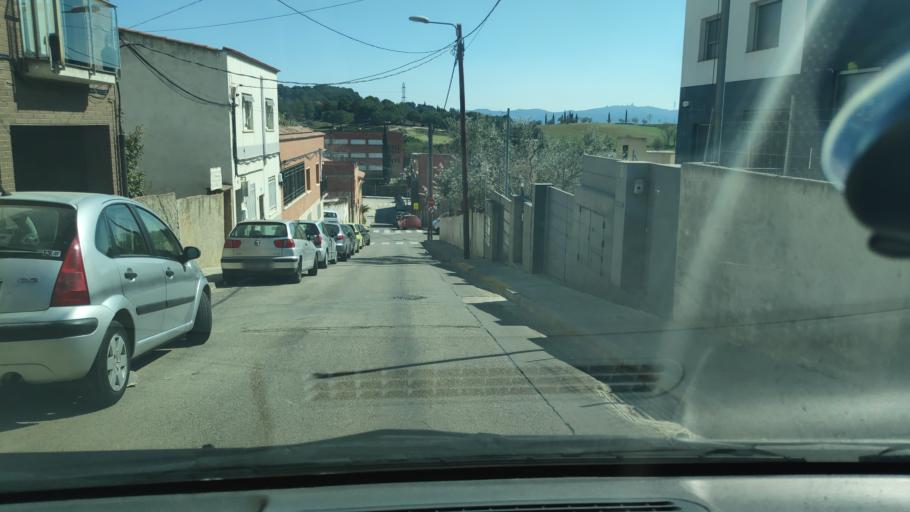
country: ES
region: Catalonia
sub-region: Provincia de Barcelona
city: Rubi
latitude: 41.4990
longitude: 2.0440
